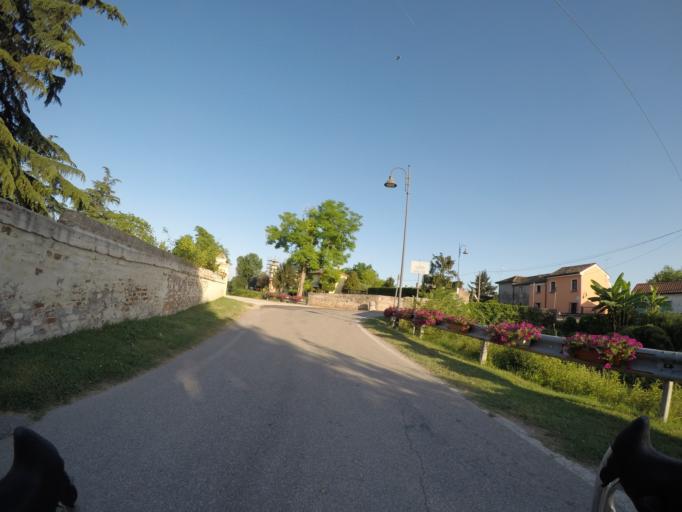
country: IT
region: Veneto
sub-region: Provincia di Rovigo
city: Villamarzana
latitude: 45.0228
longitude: 11.6771
